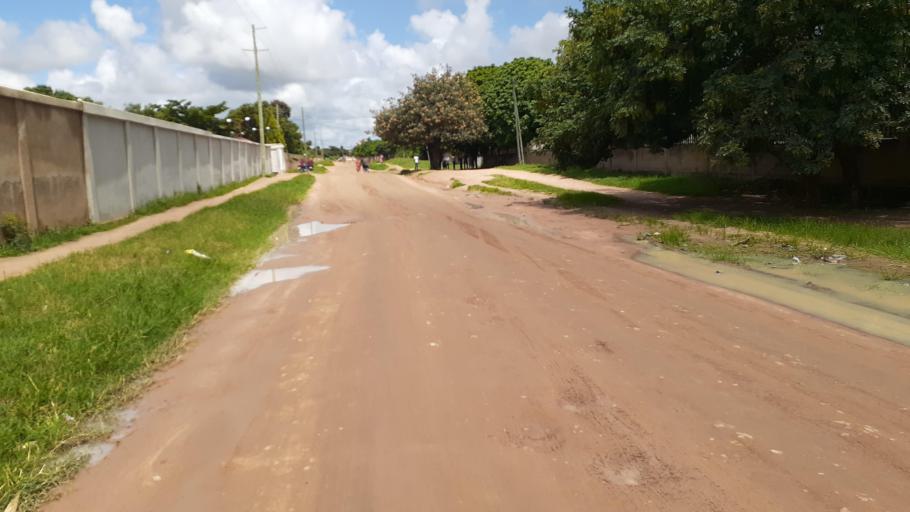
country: TZ
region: Dodoma
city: Dodoma
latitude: -6.1229
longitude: 35.7428
